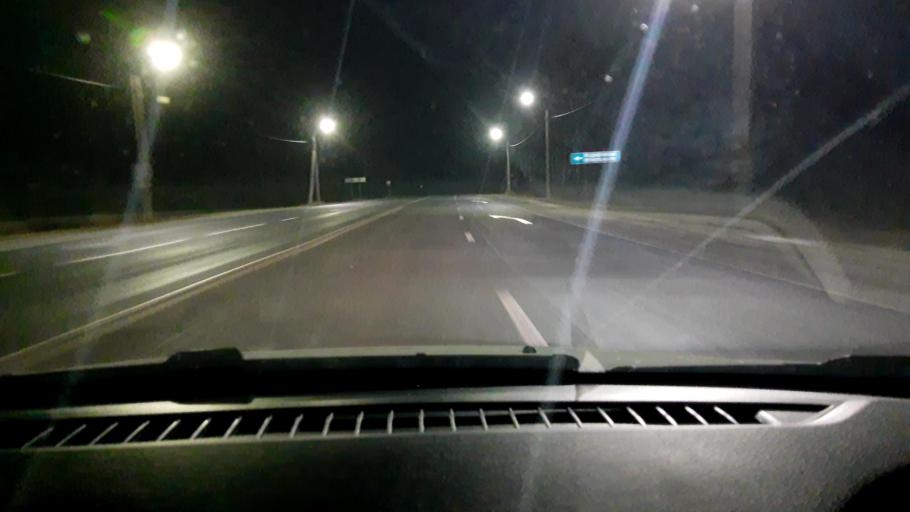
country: RU
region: Nizjnij Novgorod
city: Sitniki
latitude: 56.5073
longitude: 44.0234
